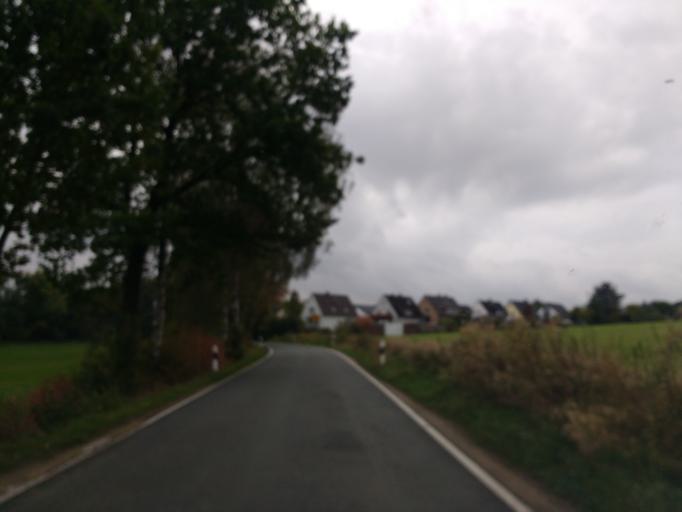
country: DE
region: North Rhine-Westphalia
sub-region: Regierungsbezirk Detmold
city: Bad Meinberg
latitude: 51.9613
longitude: 8.9488
